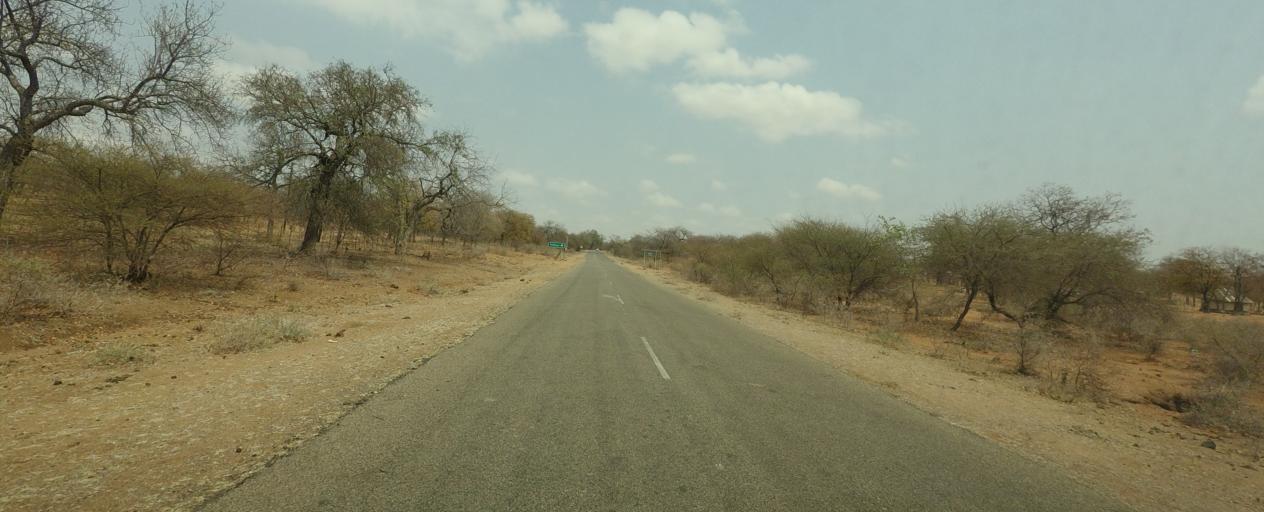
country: ZA
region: Limpopo
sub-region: Vhembe District Municipality
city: Mutale
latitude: -22.4216
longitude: 30.9455
